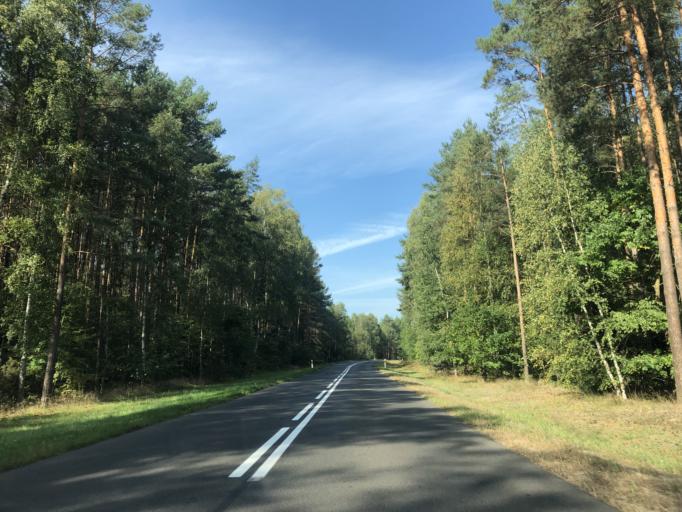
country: PL
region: Greater Poland Voivodeship
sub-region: Powiat pilski
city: Kaczory
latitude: 53.1149
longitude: 16.8356
